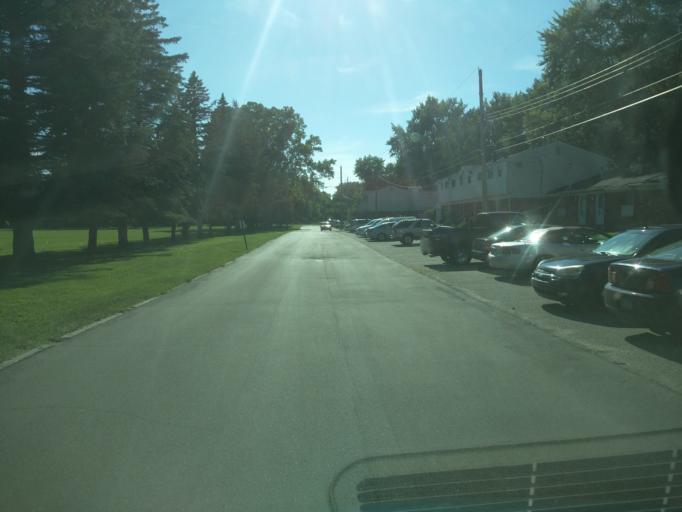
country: US
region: Michigan
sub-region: Ingham County
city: Lansing
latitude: 42.6894
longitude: -84.5849
